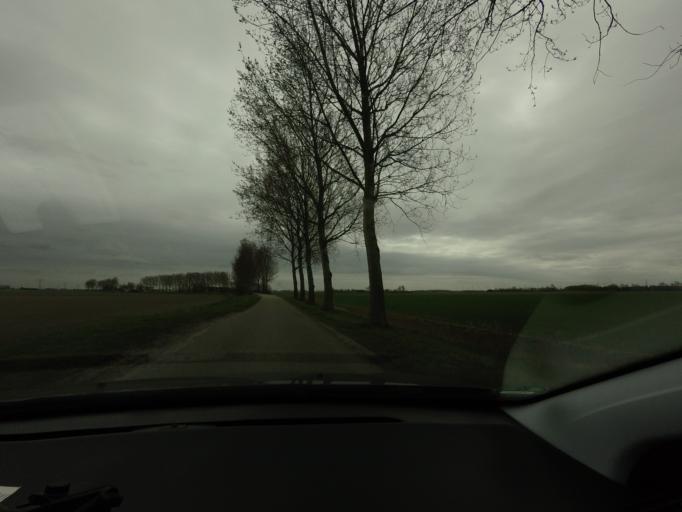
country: NL
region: South Holland
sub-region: Gemeente Goeree-Overflakkee
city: Middelharnis
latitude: 51.7333
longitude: 4.2175
